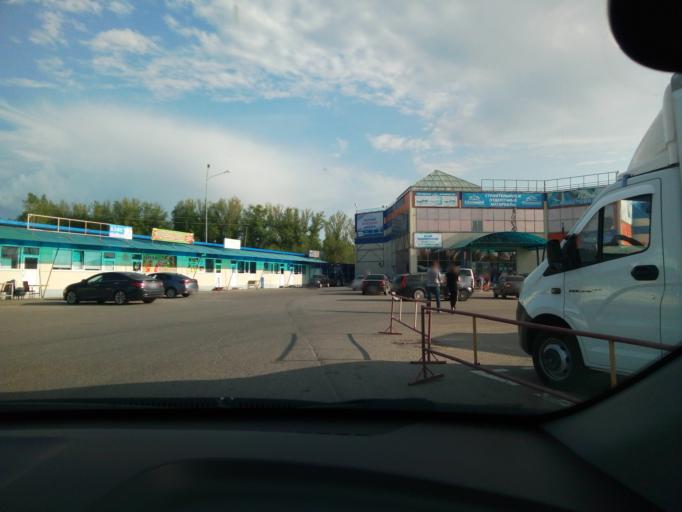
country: RU
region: Chuvashia
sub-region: Cheboksarskiy Rayon
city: Cheboksary
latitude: 56.1207
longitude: 47.2713
